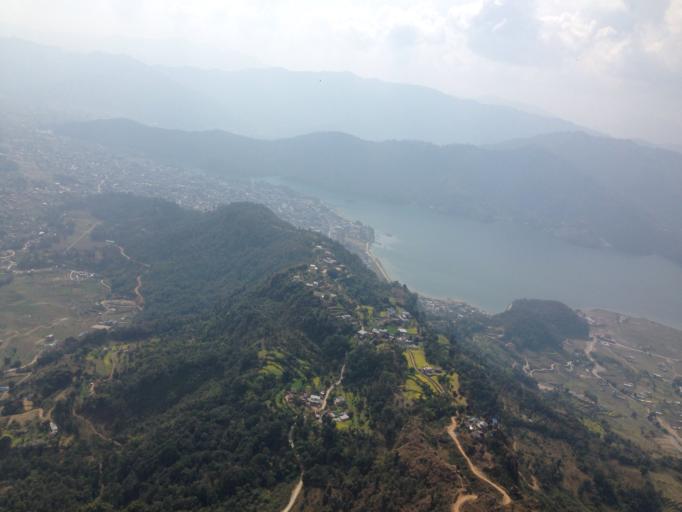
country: NP
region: Western Region
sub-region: Gandaki Zone
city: Pokhara
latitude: 28.2354
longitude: 83.9684
